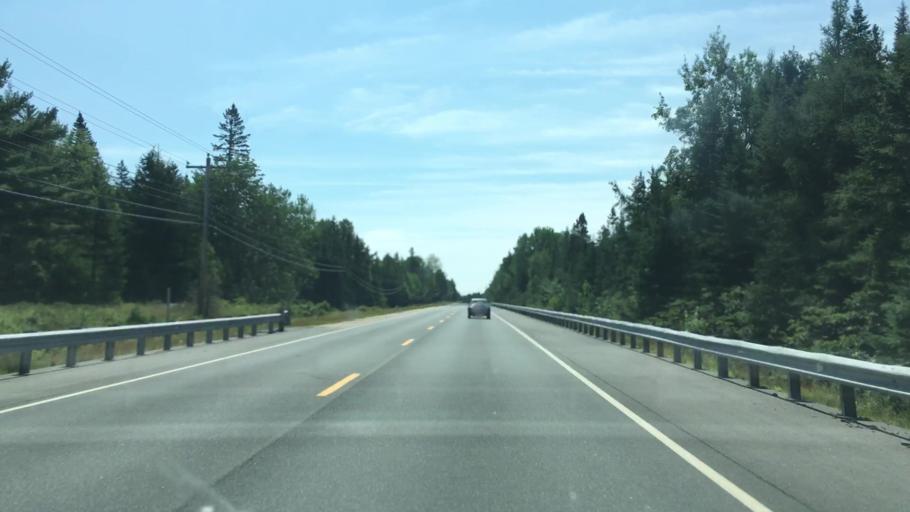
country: US
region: Maine
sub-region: Washington County
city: Calais
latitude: 45.1476
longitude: -67.1692
